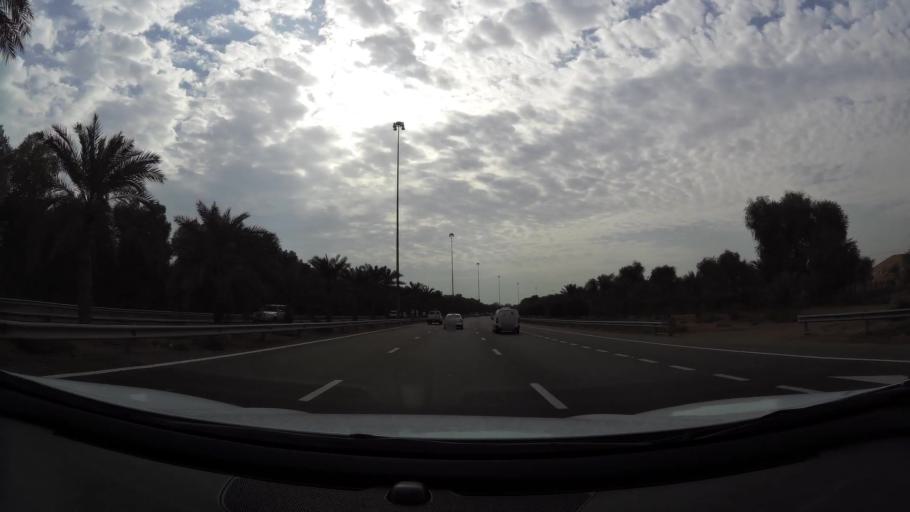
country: AE
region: Abu Dhabi
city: Al Ain
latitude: 24.1991
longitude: 55.5855
